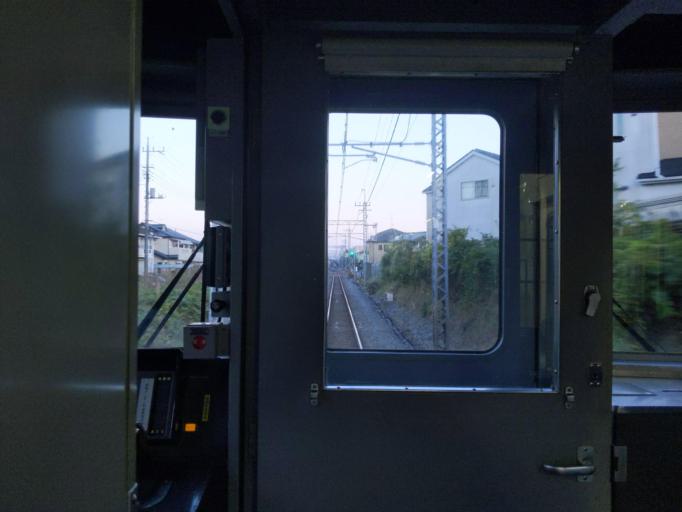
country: JP
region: Chiba
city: Noda
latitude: 35.9383
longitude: 139.8816
